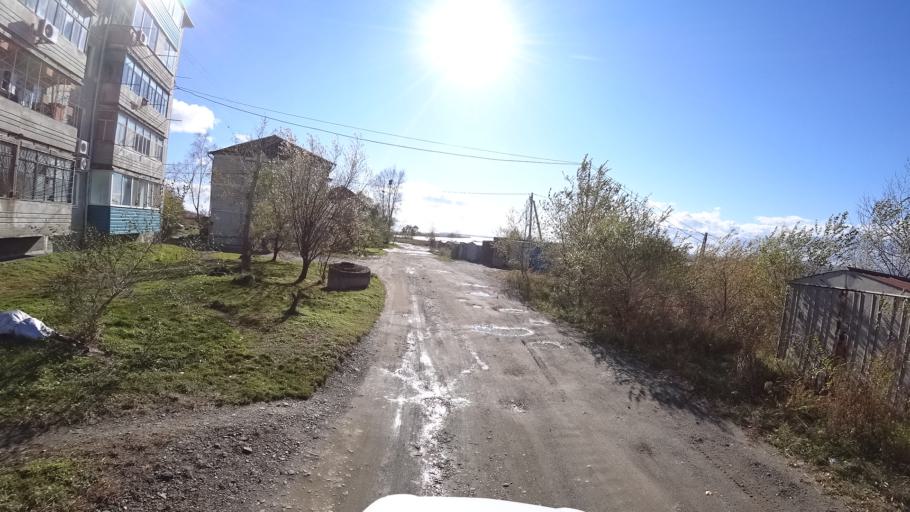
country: RU
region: Khabarovsk Krai
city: Amursk
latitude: 50.2172
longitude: 136.8893
